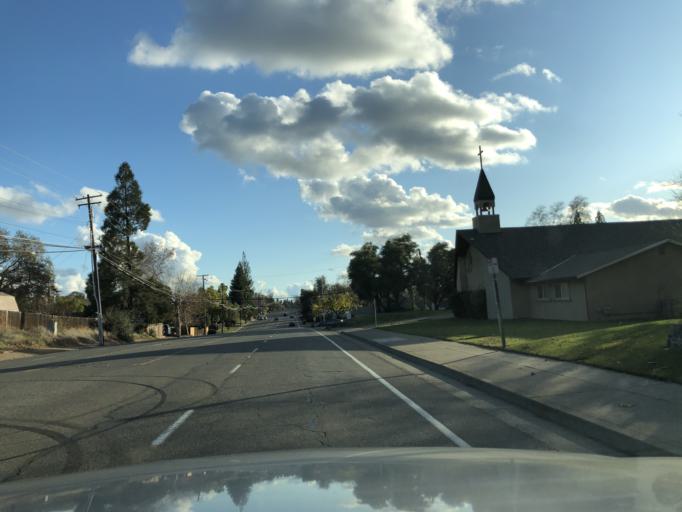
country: US
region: California
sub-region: Sacramento County
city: Fair Oaks
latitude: 38.6613
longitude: -121.3086
